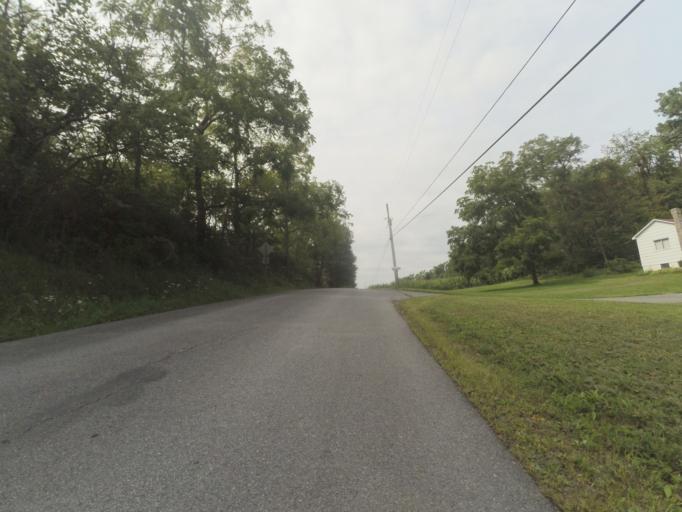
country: US
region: Pennsylvania
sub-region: Huntingdon County
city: Huntingdon
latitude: 40.5878
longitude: -78.0704
